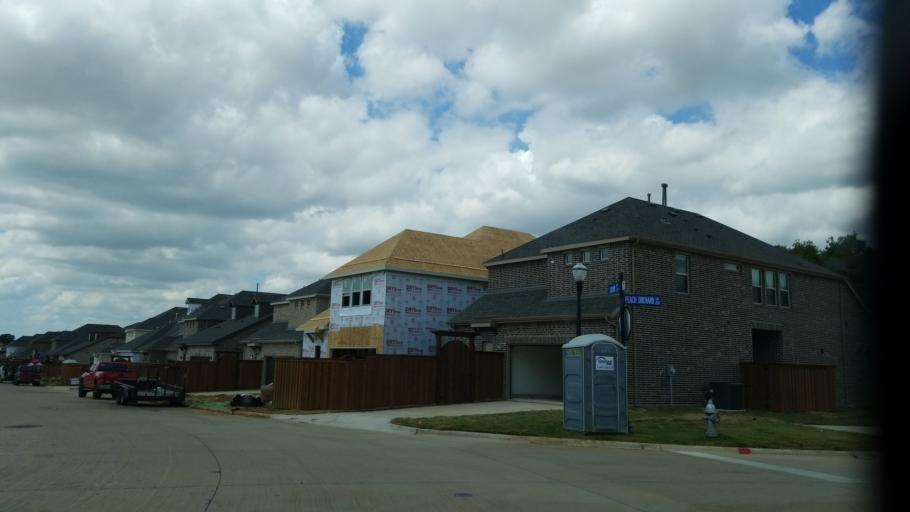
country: US
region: Texas
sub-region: Tarrant County
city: Euless
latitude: 32.8344
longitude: -97.0943
